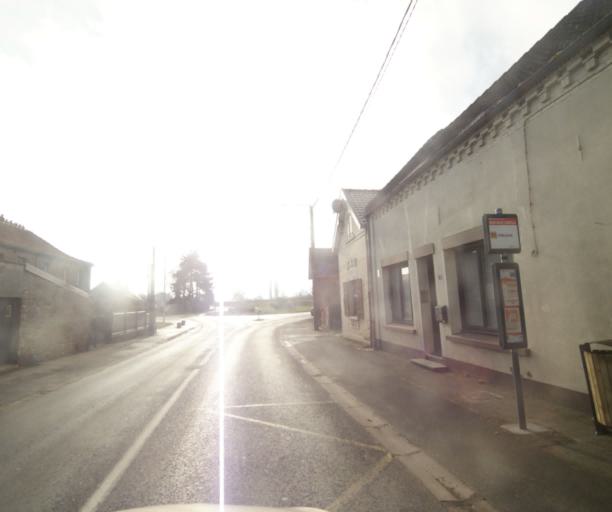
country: FR
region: Nord-Pas-de-Calais
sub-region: Departement du Nord
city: Thiant
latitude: 50.2860
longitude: 3.4490
